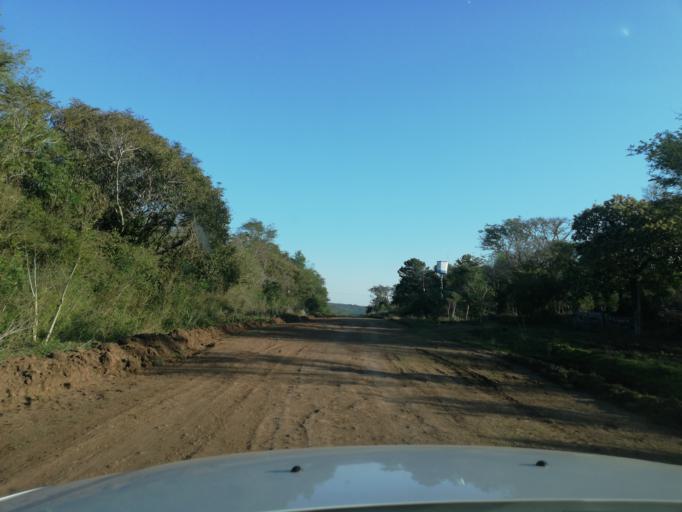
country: AR
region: Misiones
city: Cerro Cora
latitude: -27.5843
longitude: -55.6877
